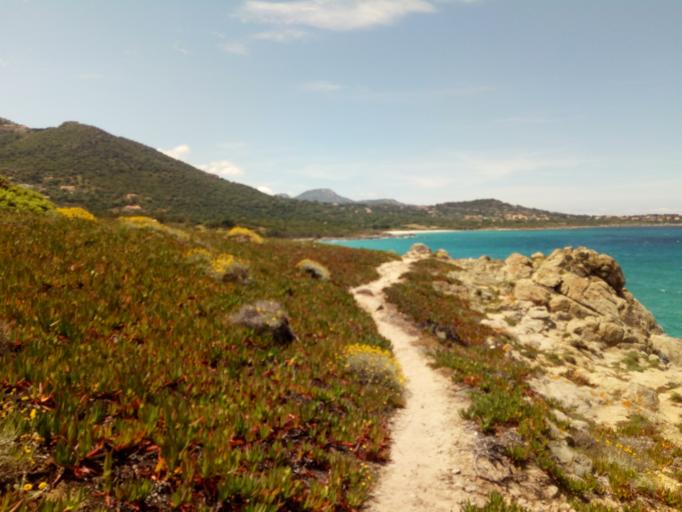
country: FR
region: Corsica
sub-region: Departement de la Haute-Corse
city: L'Ile-Rousse
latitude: 42.6327
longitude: 8.9151
